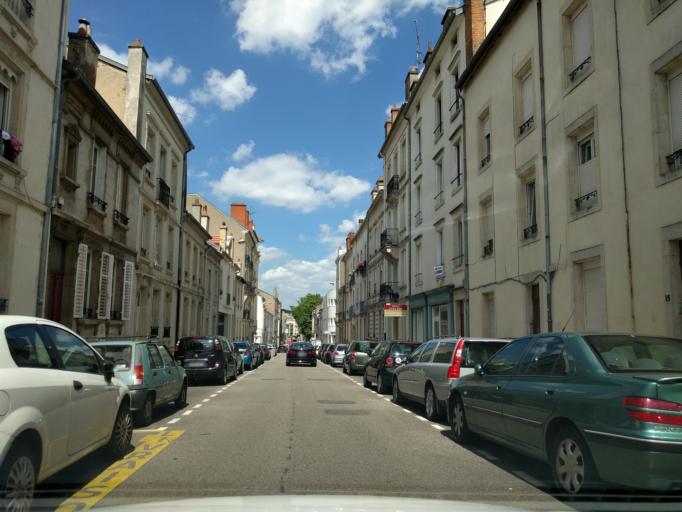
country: FR
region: Lorraine
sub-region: Departement de Meurthe-et-Moselle
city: Nancy
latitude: 48.6832
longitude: 6.1715
